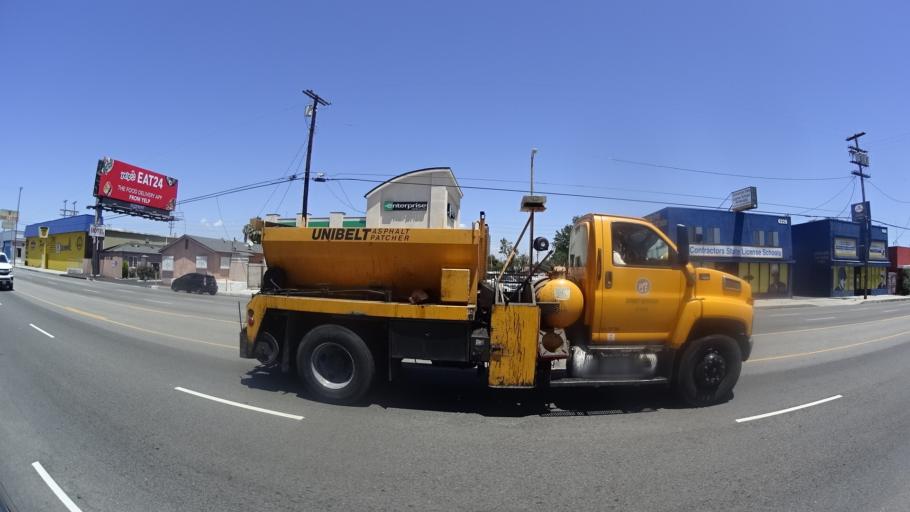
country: US
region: California
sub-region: Los Angeles County
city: Van Nuys
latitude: 34.1840
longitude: -118.4664
